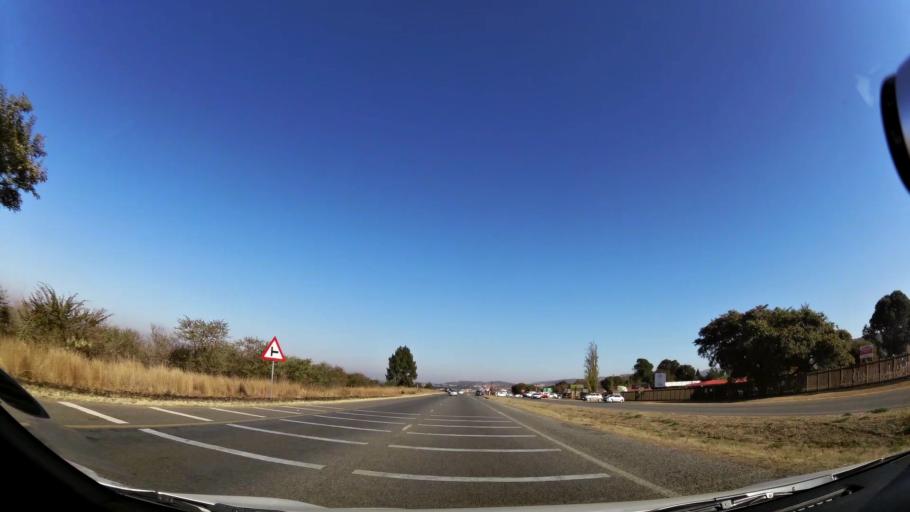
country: ZA
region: Gauteng
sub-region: City of Johannesburg Metropolitan Municipality
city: Johannesburg
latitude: -26.3126
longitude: 28.0811
